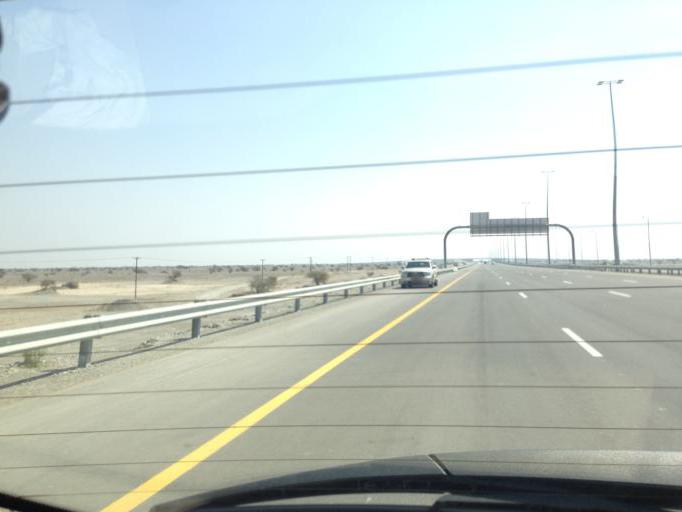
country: OM
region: Al Batinah
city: Barka'
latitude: 23.5759
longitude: 57.7527
